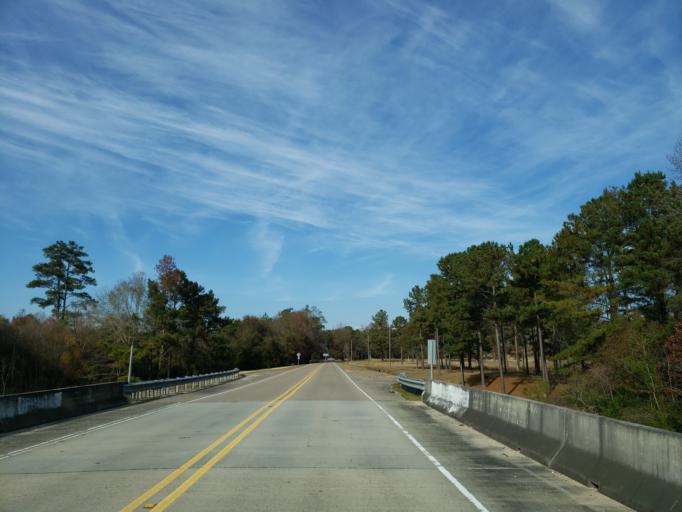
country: US
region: Mississippi
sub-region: Forrest County
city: Rawls Springs
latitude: 31.3972
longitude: -89.3651
